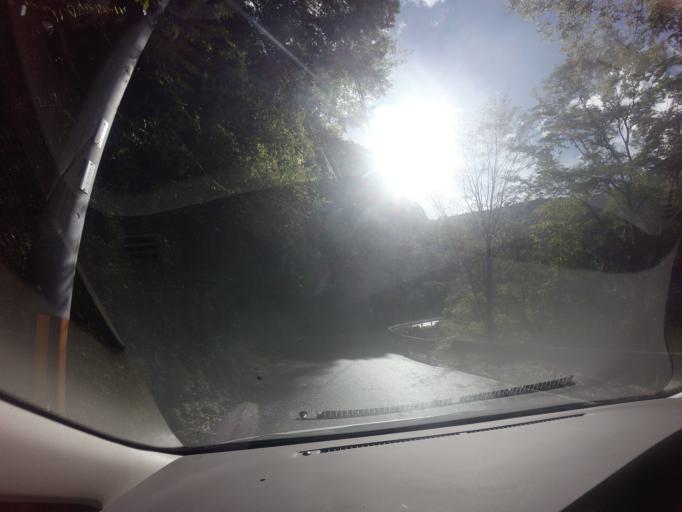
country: JP
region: Wakayama
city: Shingu
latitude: 33.9626
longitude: 135.8485
